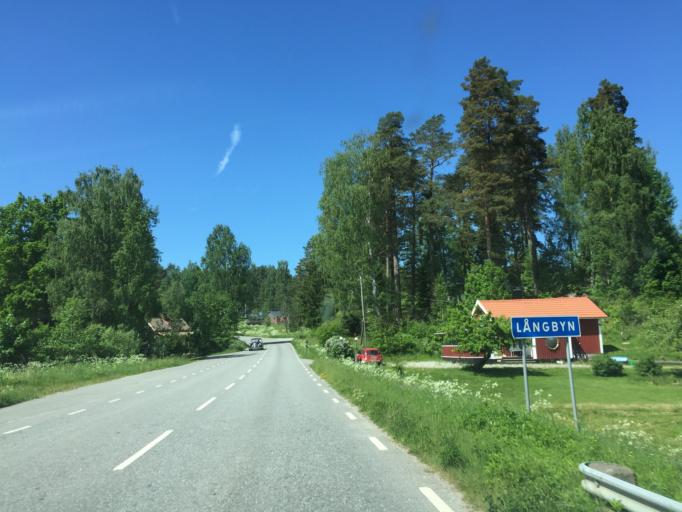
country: SE
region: OErebro
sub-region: Orebro Kommun
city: Hovsta
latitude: 59.3850
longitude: 15.2068
